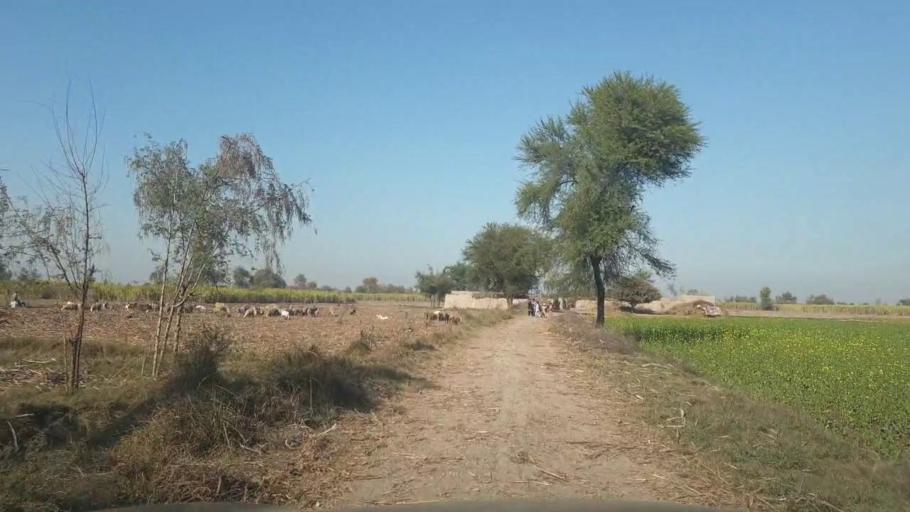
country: PK
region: Sindh
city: Mirpur Mathelo
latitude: 27.9938
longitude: 69.4769
